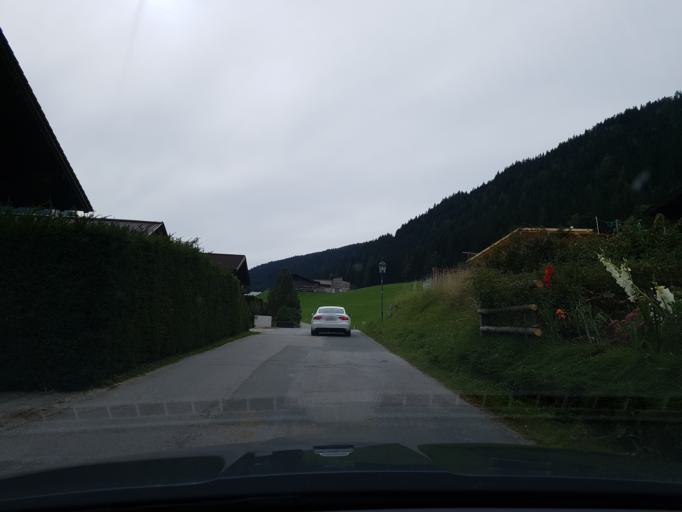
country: AT
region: Salzburg
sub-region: Politischer Bezirk Sankt Johann im Pongau
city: Forstau
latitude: 47.3748
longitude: 13.5498
